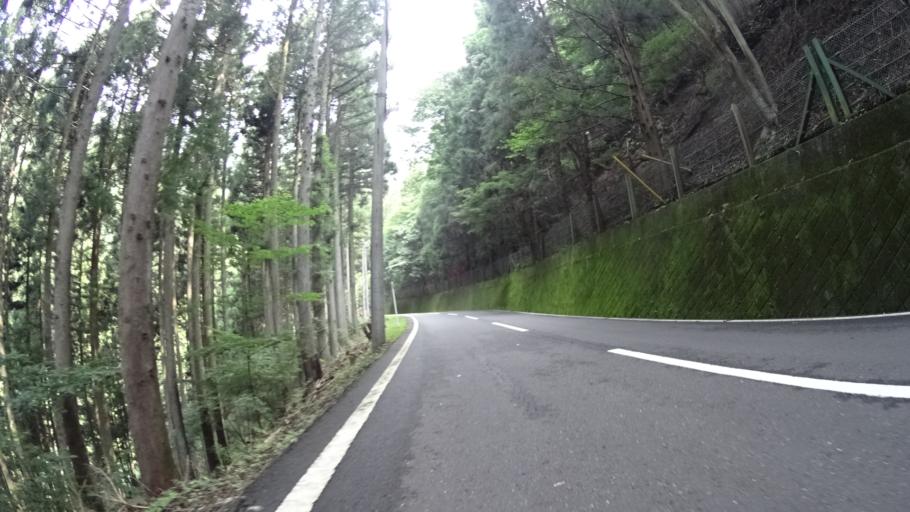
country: JP
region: Gunma
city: Tomioka
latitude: 36.0616
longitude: 138.8529
